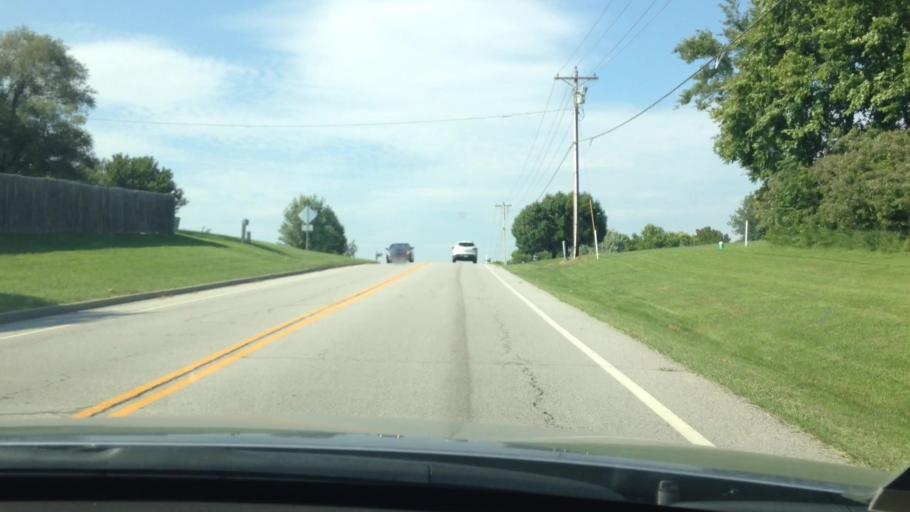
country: US
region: Missouri
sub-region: Platte County
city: Platte City
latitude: 39.3337
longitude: -94.7611
